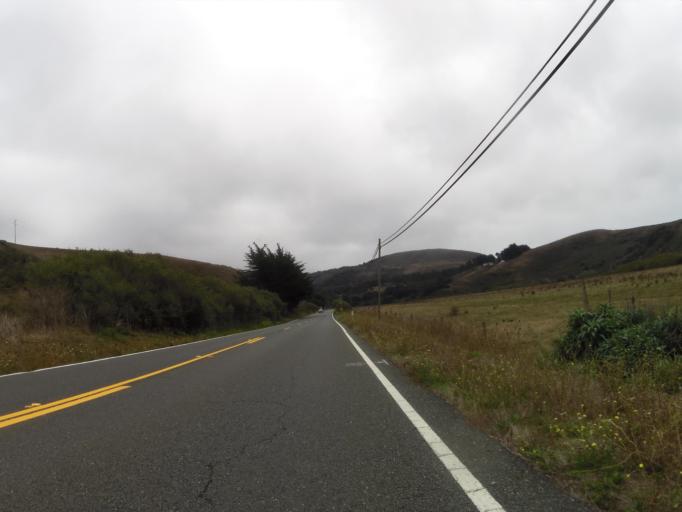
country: US
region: California
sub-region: Sonoma County
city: Monte Rio
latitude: 38.4418
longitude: -123.1092
